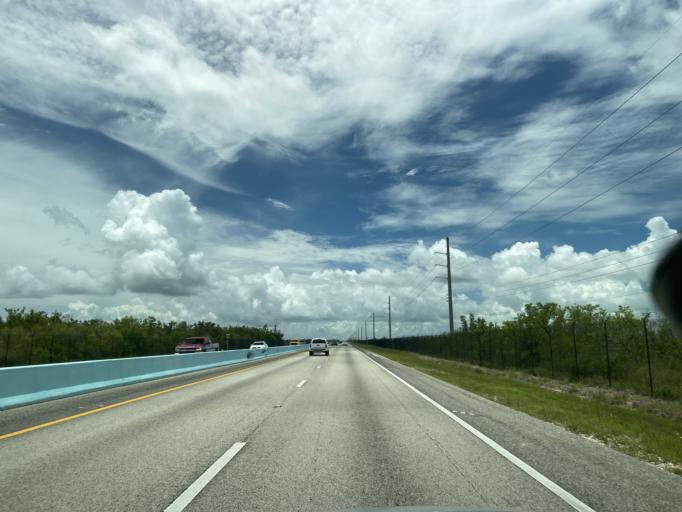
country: US
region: Florida
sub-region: Miami-Dade County
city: Florida City
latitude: 25.3520
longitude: -80.4584
